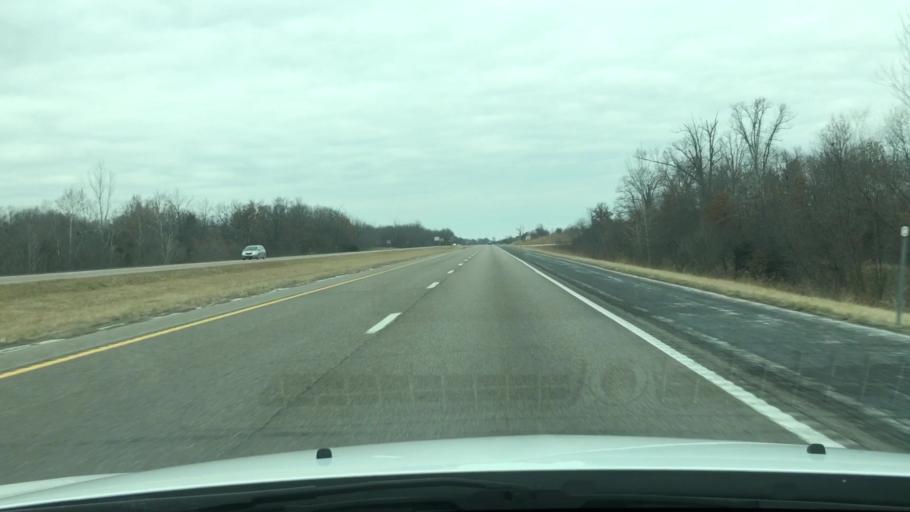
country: US
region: Missouri
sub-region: Callaway County
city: Fulton
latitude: 38.9863
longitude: -91.8938
